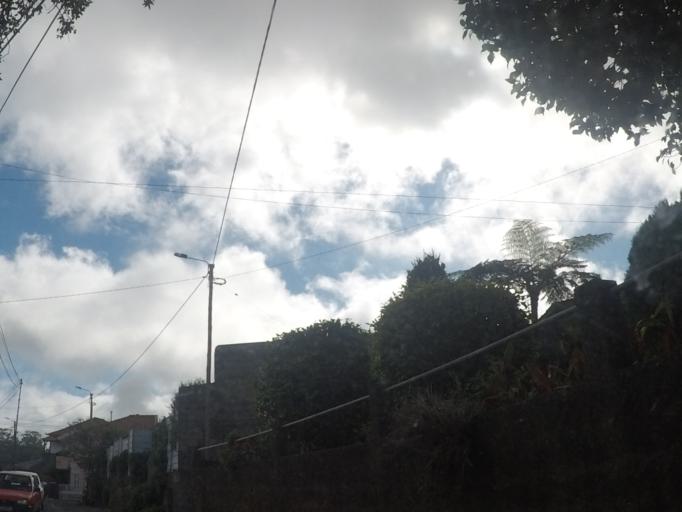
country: PT
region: Madeira
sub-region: Santa Cruz
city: Camacha
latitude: 32.6834
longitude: -16.8538
